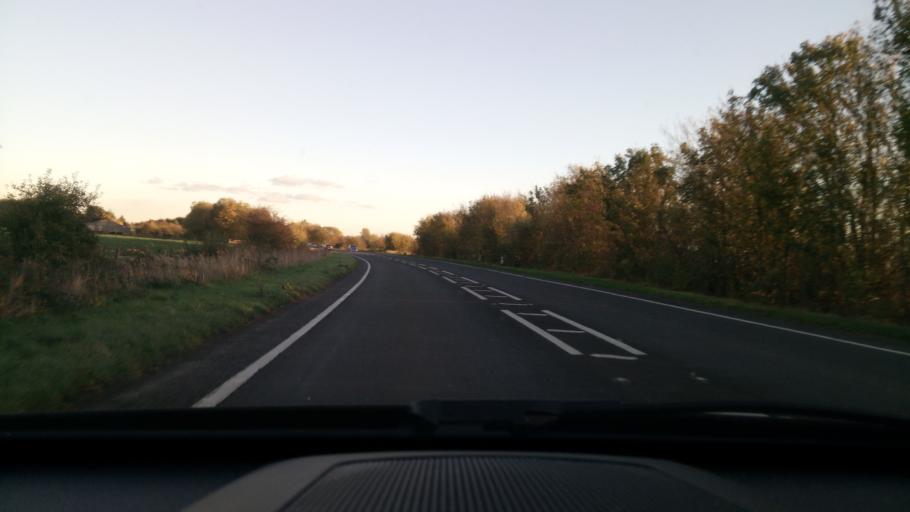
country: GB
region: England
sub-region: Peterborough
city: Glinton
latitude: 52.6341
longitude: -0.3053
